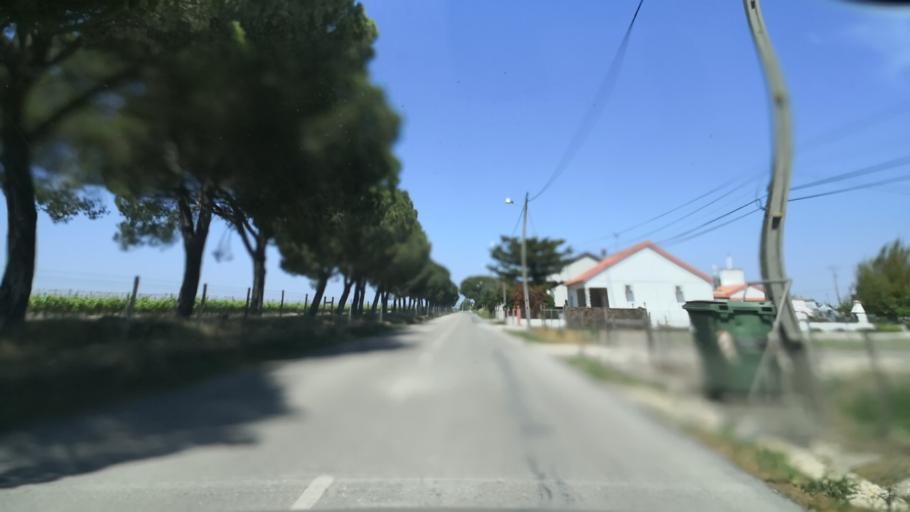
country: PT
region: Santarem
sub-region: Benavente
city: Poceirao
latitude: 38.6765
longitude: -8.7339
